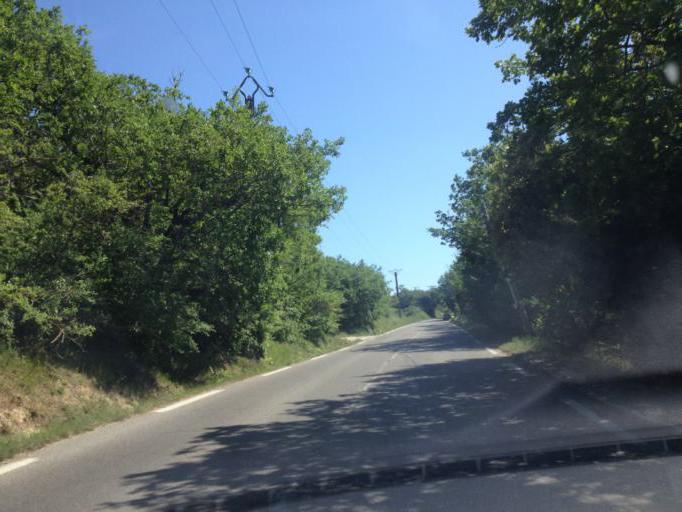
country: FR
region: Provence-Alpes-Cote d'Azur
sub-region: Departement du Vaucluse
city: Lourmarin
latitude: 43.7544
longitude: 5.3653
